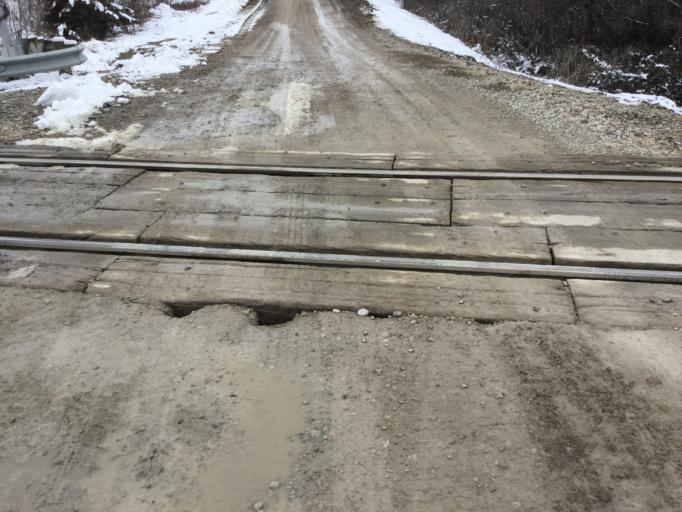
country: US
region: Kansas
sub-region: Osage County
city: Carbondale
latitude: 38.9135
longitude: -95.6983
